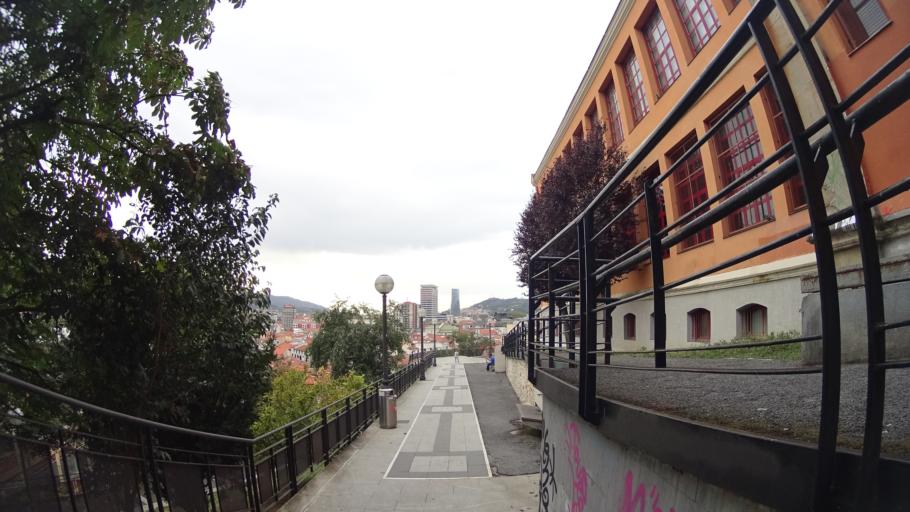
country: ES
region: Basque Country
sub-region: Bizkaia
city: Santutxu
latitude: 43.2571
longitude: -2.9211
